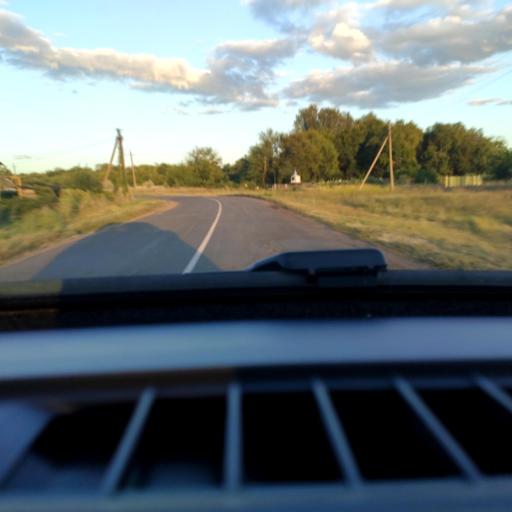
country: RU
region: Voronezj
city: Orlovo
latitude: 51.6134
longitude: 39.8092
